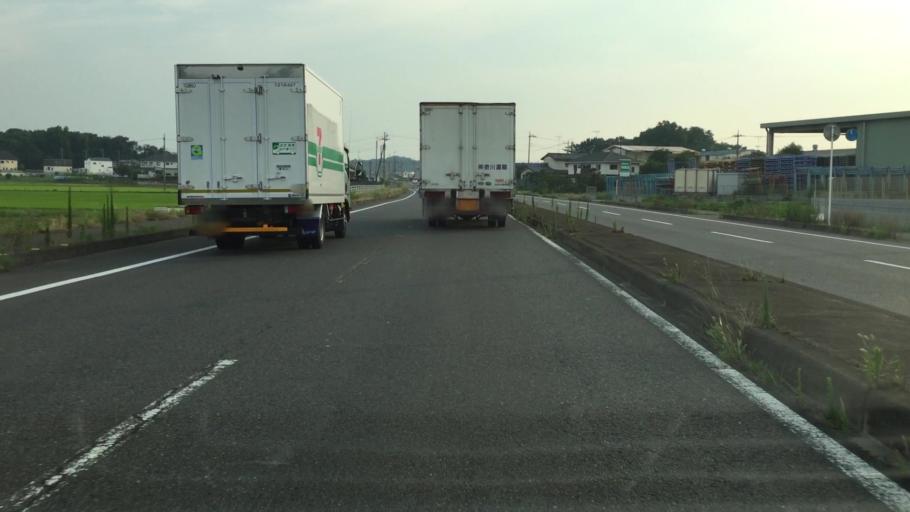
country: JP
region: Tochigi
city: Tochigi
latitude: 36.3279
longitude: 139.6858
